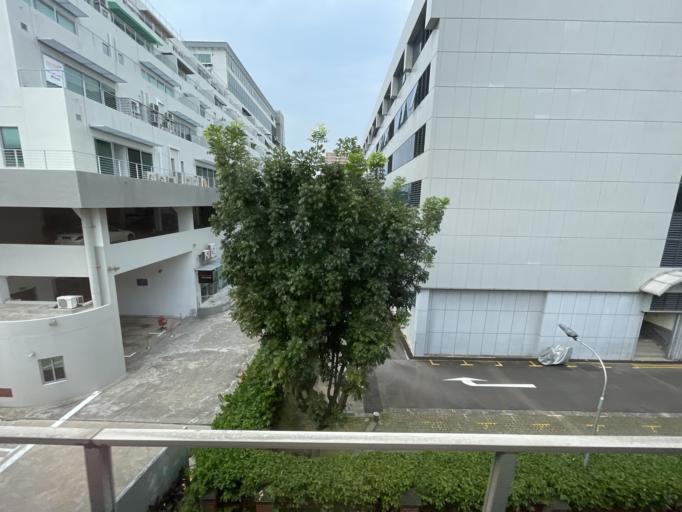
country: SG
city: Singapore
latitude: 1.2907
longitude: 103.8140
